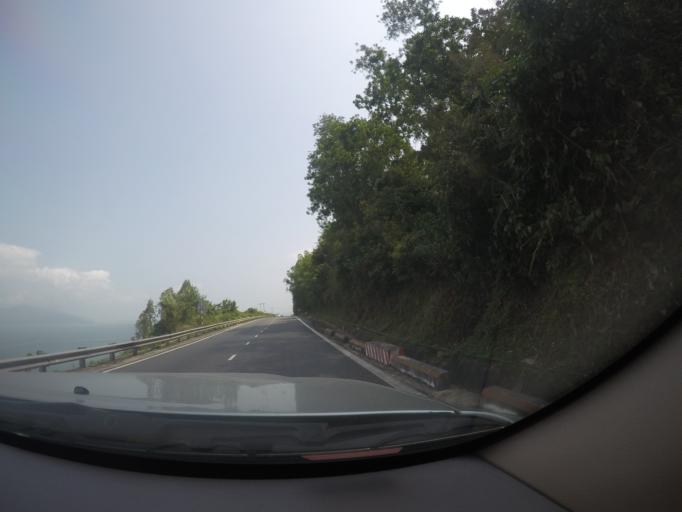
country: VN
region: Da Nang
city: Lien Chieu
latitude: 16.1516
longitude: 108.1332
